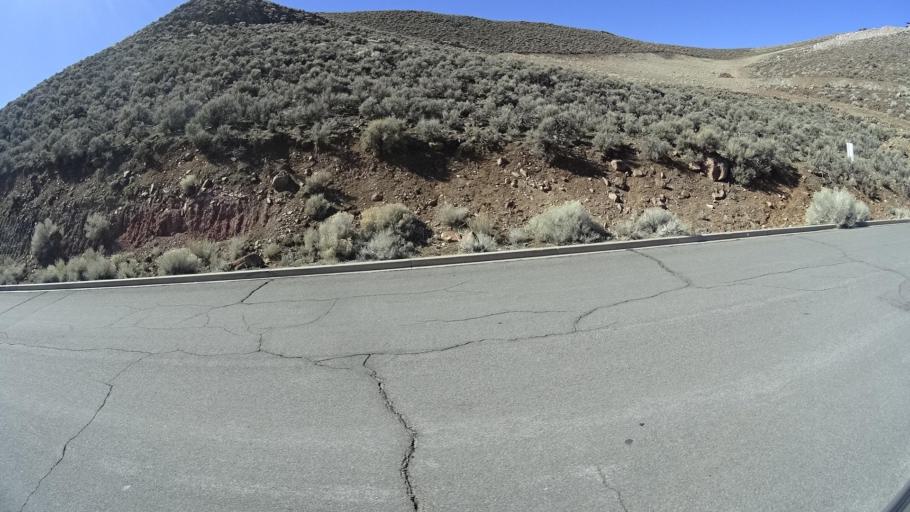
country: US
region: Nevada
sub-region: Washoe County
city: Sparks
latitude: 39.4781
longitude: -119.7262
